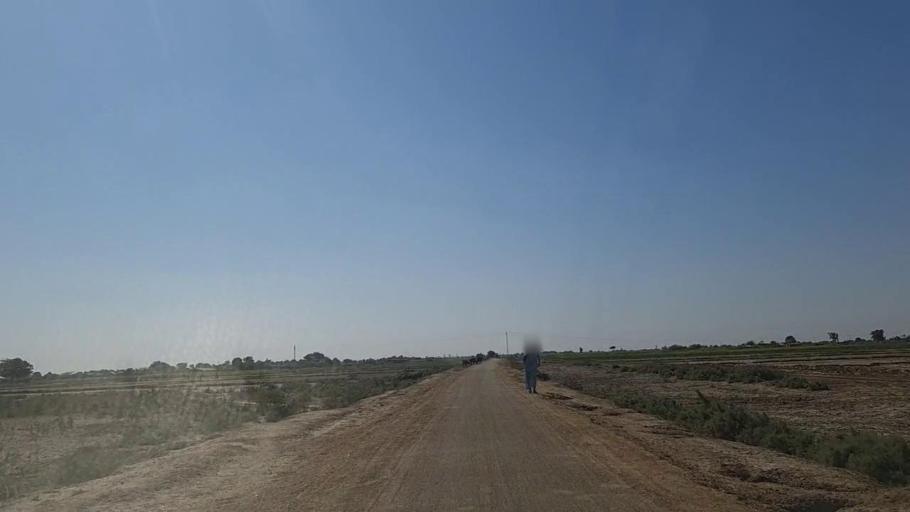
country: PK
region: Sindh
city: Samaro
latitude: 25.0832
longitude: 69.3909
